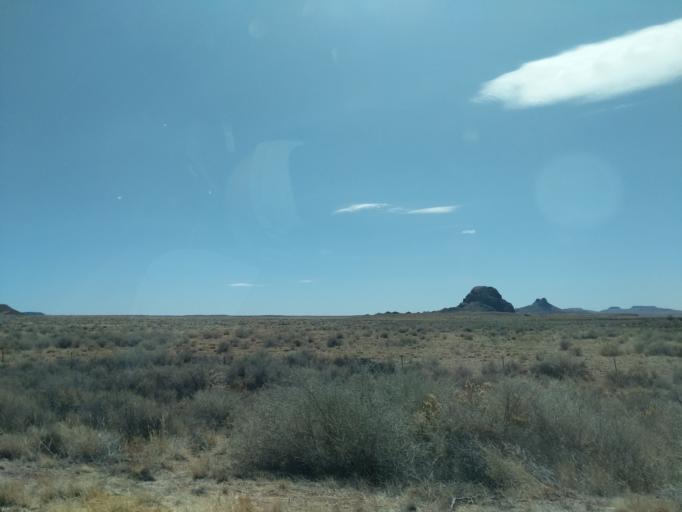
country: US
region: Arizona
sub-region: Navajo County
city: Dilkon
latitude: 35.3981
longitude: -110.0709
